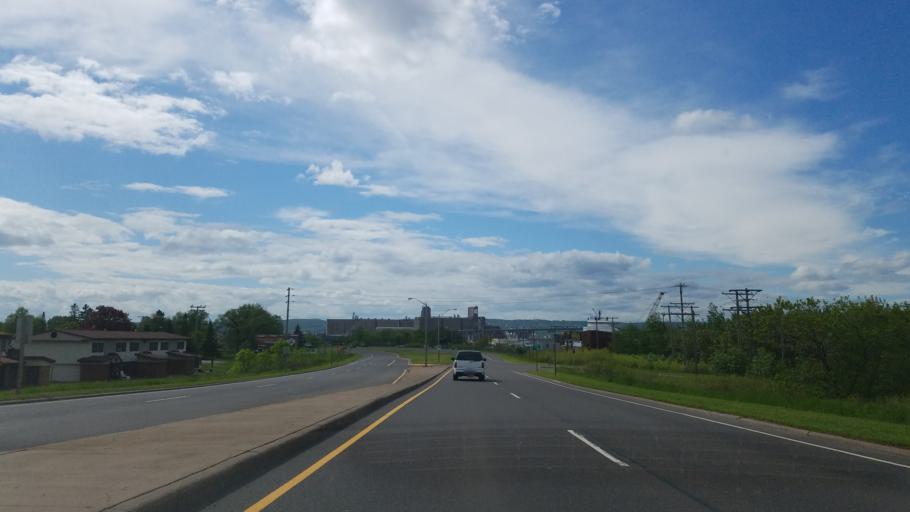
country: US
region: Wisconsin
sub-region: Douglas County
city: Superior
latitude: 46.7318
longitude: -92.0836
